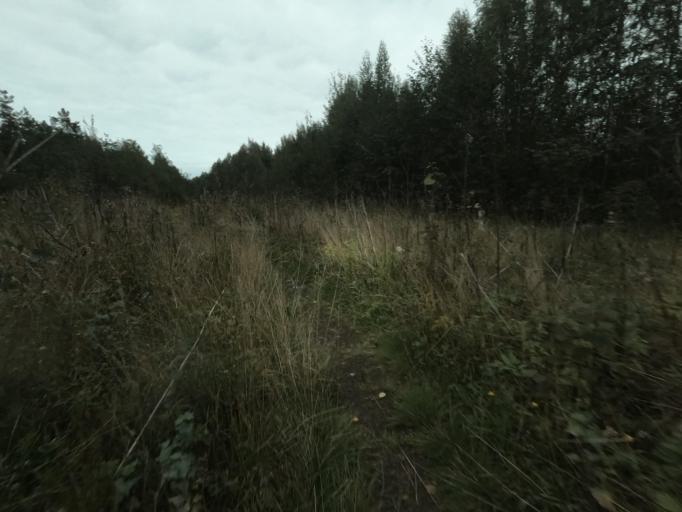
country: RU
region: St.-Petersburg
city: Sapernyy
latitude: 59.7659
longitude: 30.7285
